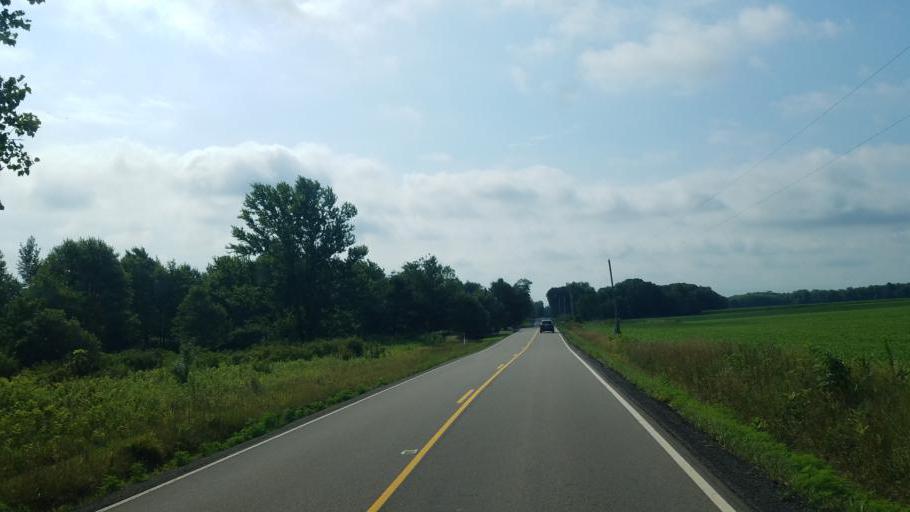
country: US
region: Ohio
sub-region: Knox County
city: Centerburg
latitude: 40.3031
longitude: -82.6448
